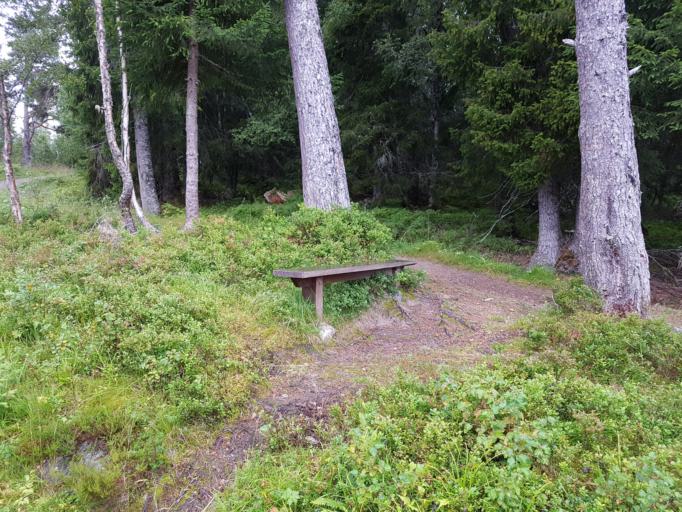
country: NO
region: Sor-Trondelag
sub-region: Trondheim
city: Trondheim
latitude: 63.4200
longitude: 10.2824
